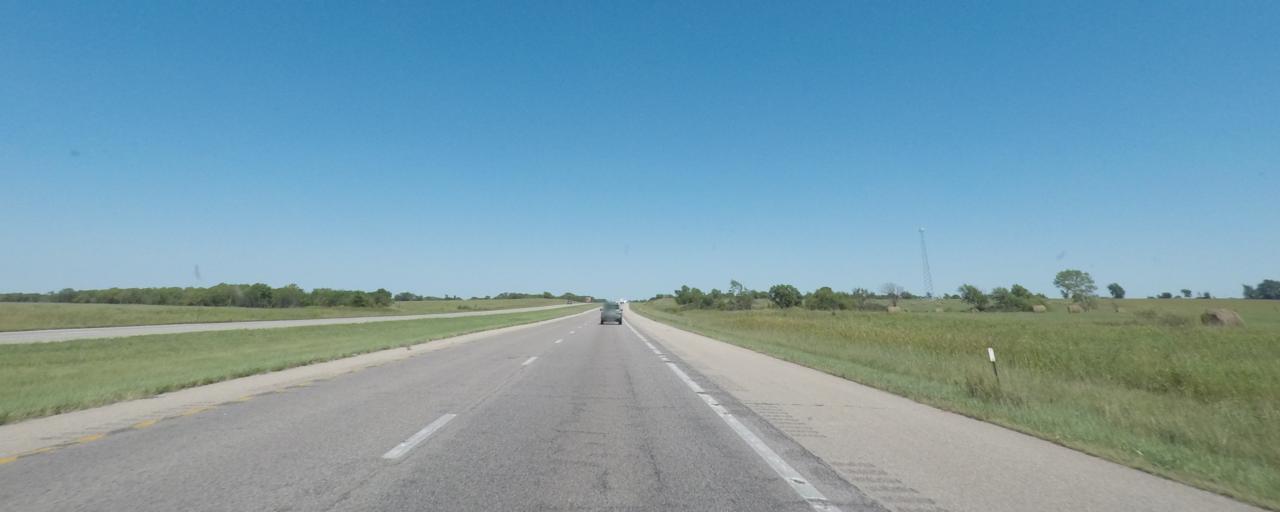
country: US
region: Kansas
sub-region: Osage County
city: Osage City
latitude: 38.4201
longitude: -95.9120
